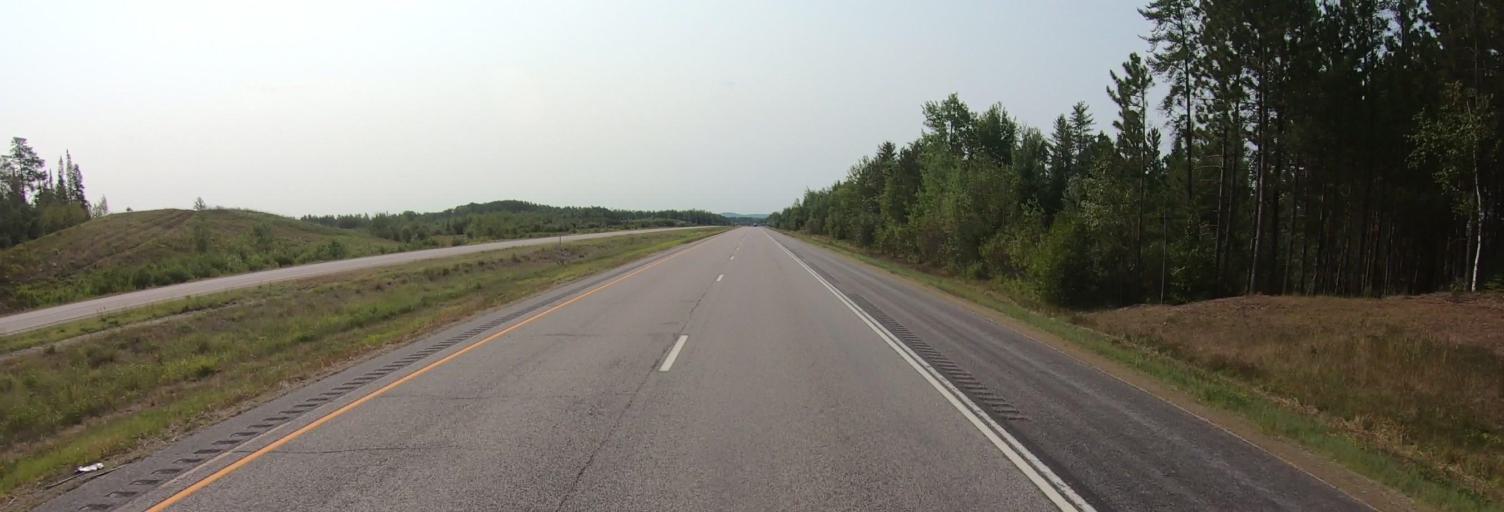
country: US
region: Minnesota
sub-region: Saint Louis County
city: Parkville
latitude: 47.6484
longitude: -92.5678
